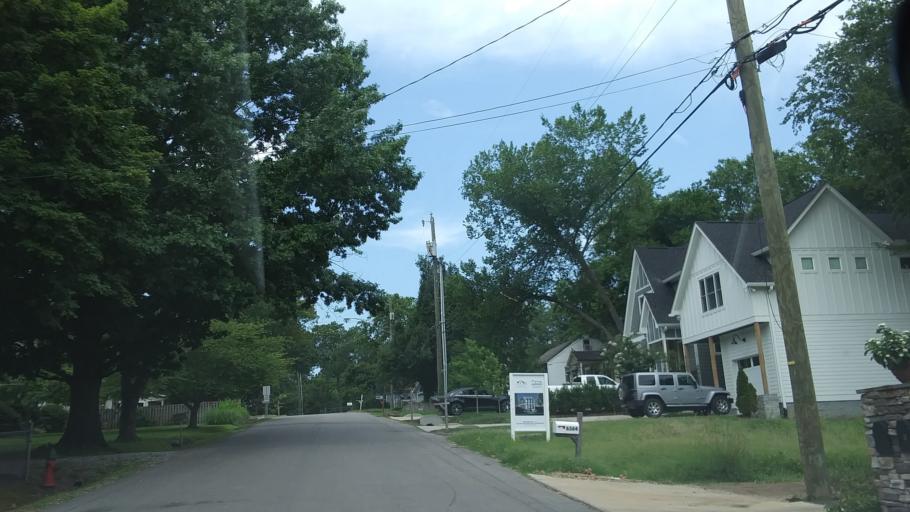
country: US
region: Tennessee
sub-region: Davidson County
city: Belle Meade
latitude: 36.1531
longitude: -86.8733
